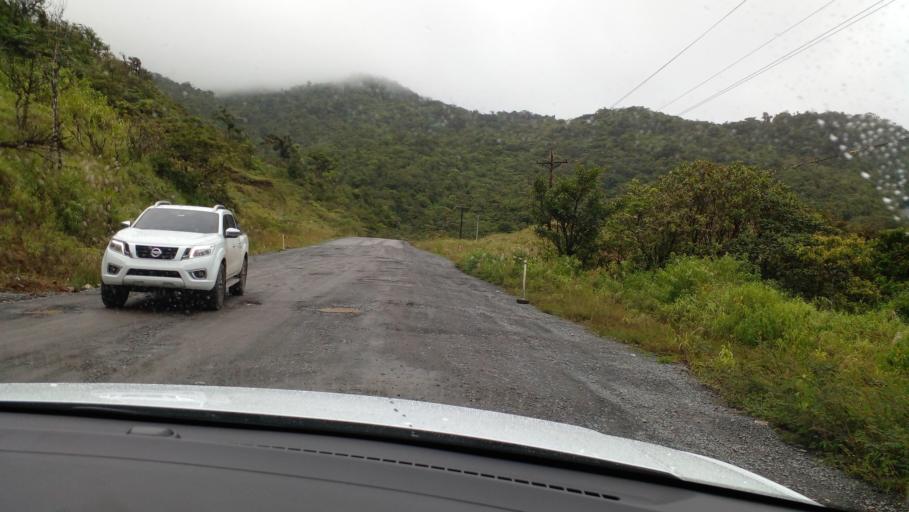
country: PA
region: Chiriqui
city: Gualaca
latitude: 8.7044
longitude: -82.2303
